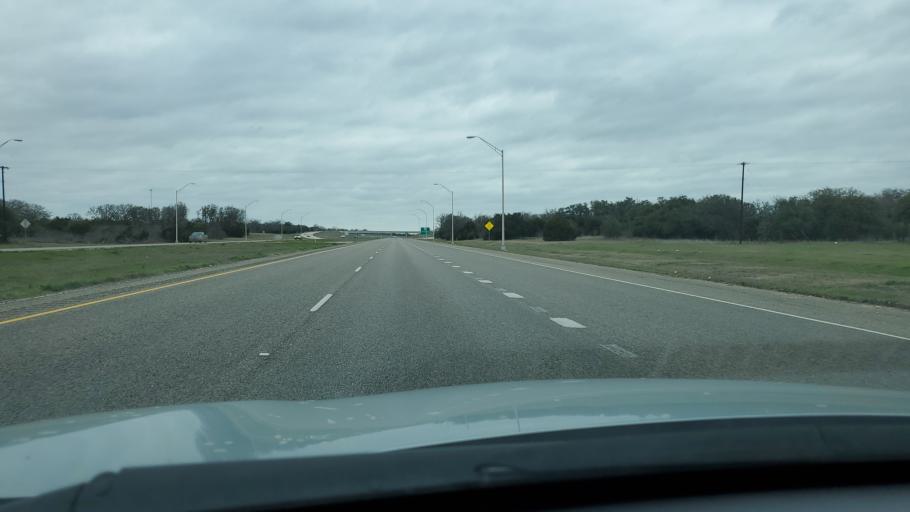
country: US
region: Texas
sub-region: Williamson County
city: Florence
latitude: 30.8488
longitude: -97.7887
